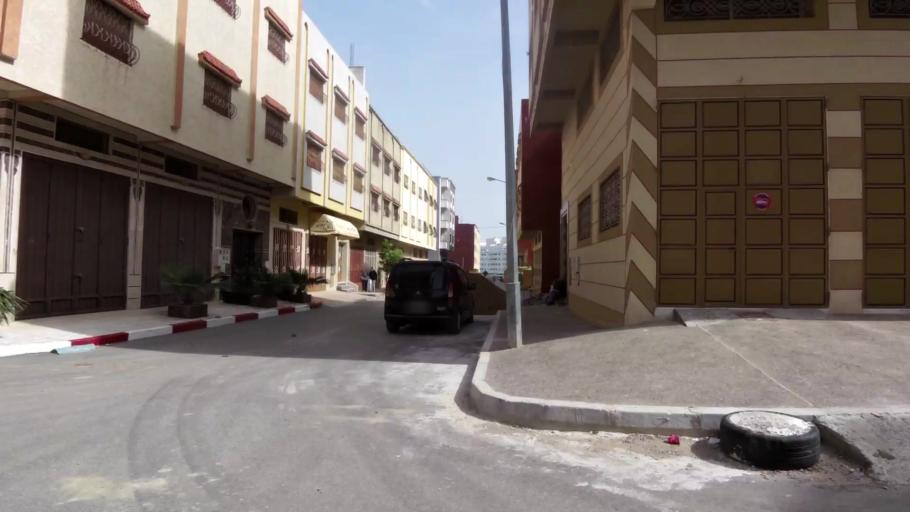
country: MA
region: Tanger-Tetouan
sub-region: Tanger-Assilah
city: Boukhalef
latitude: 35.7471
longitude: -5.8584
